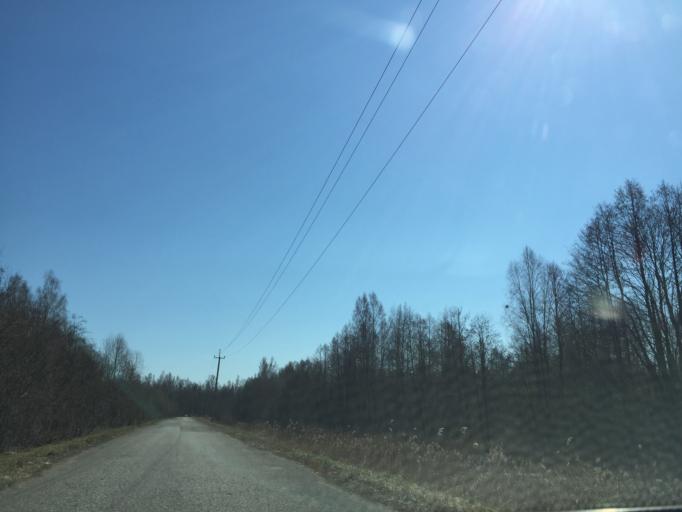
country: EE
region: Jogevamaa
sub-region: Mustvee linn
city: Mustvee
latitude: 58.7733
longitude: 26.9457
